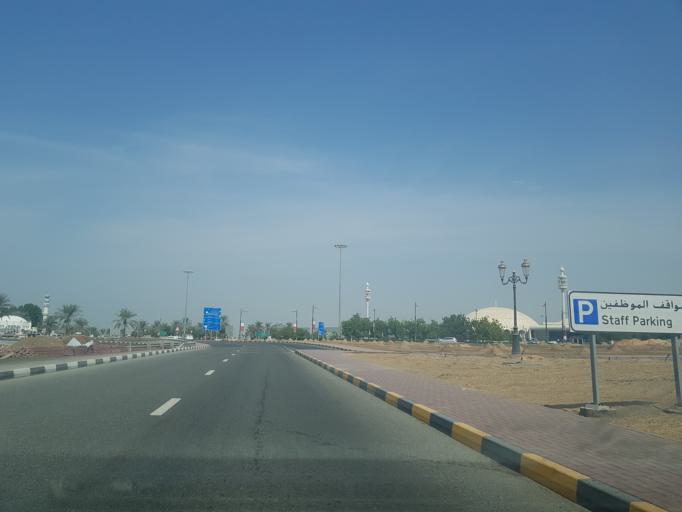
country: AE
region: Ash Shariqah
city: Sharjah
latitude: 25.3180
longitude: 55.5203
